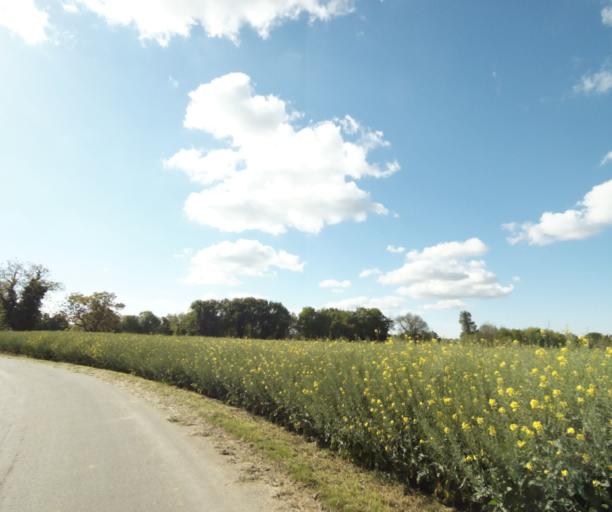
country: FR
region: Poitou-Charentes
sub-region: Departement de la Charente-Maritime
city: Nieul-les-Saintes
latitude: 45.7065
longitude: -0.7419
